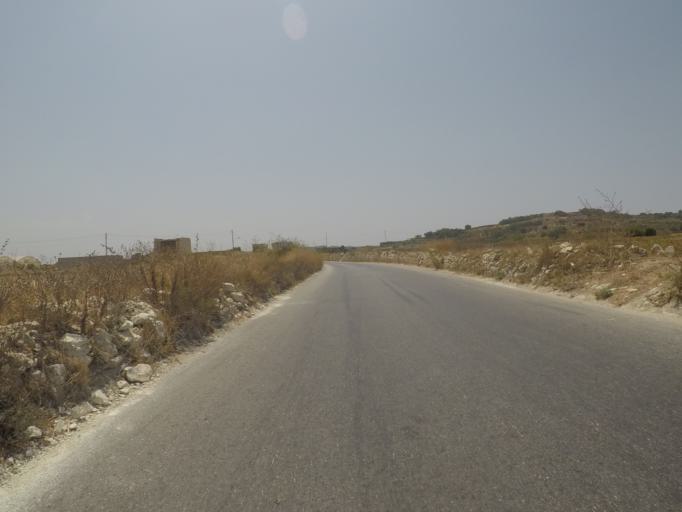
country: MT
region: Ir-Rabat
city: Rabat
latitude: 35.8723
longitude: 14.4140
